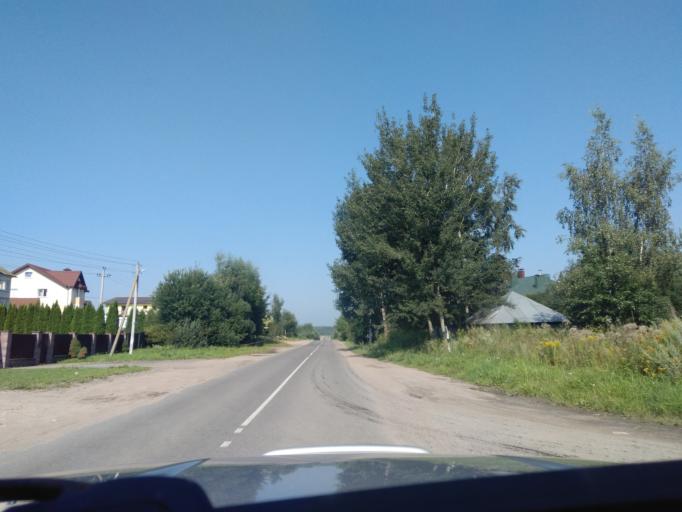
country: BY
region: Minsk
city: Zhdanovichy
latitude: 53.9325
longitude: 27.4135
